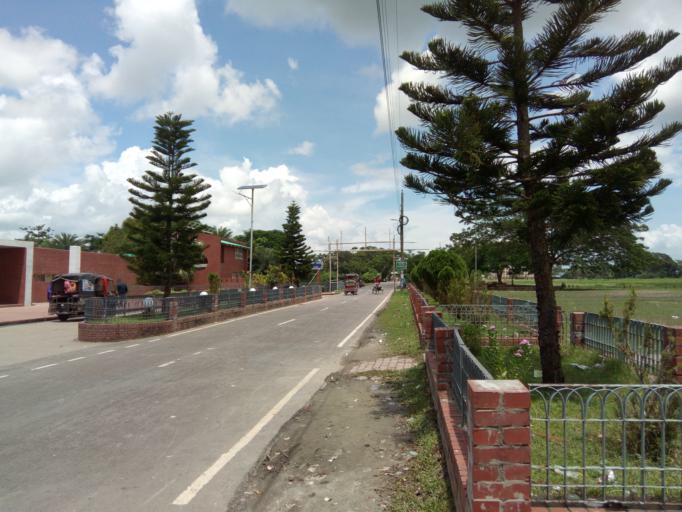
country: BD
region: Dhaka
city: Tungipara
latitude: 22.9039
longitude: 89.8990
